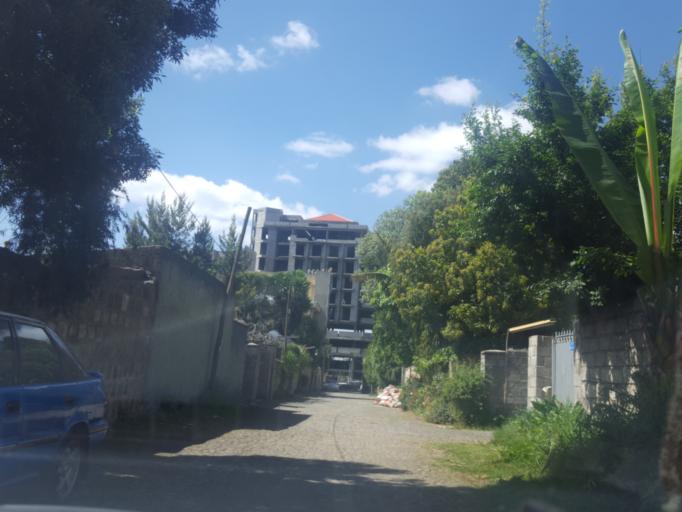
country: ET
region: Adis Abeba
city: Addis Ababa
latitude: 9.0560
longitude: 38.7424
